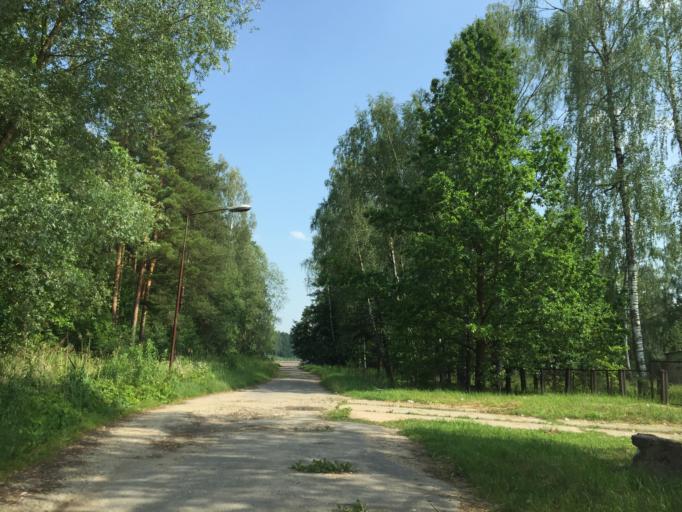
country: LV
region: Ozolnieku
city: Ozolnieki
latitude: 56.6734
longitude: 23.7629
